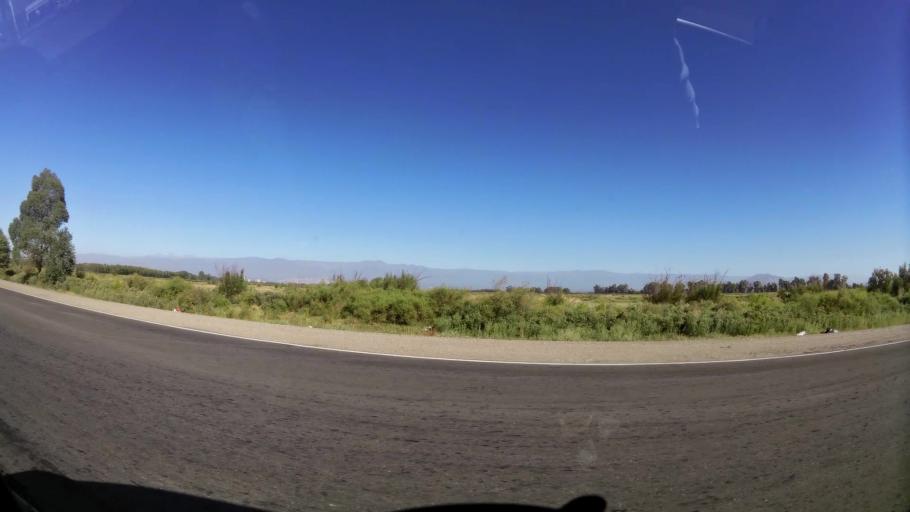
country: AR
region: Mendoza
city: General Lavalle
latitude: -32.7159
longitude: -68.6800
